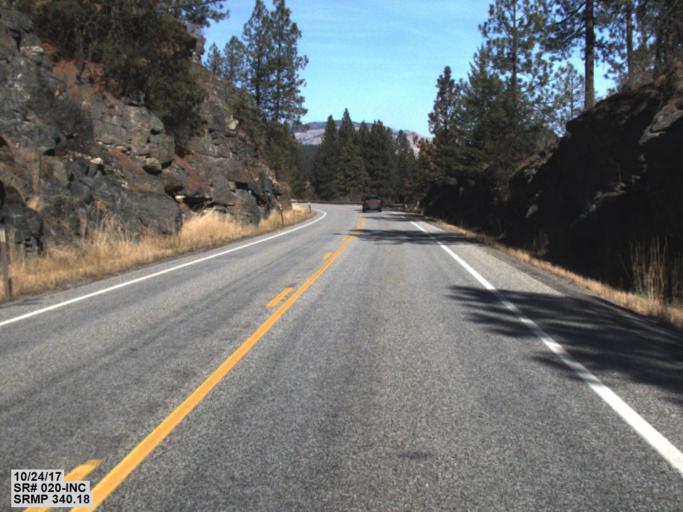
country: US
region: Washington
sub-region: Stevens County
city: Kettle Falls
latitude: 48.6046
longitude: -118.1391
